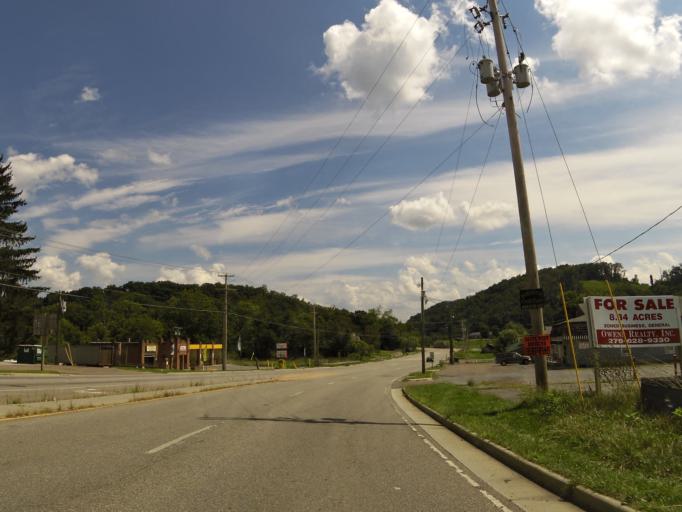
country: US
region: Virginia
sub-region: Washington County
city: Abingdon
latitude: 36.7121
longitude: -81.9274
